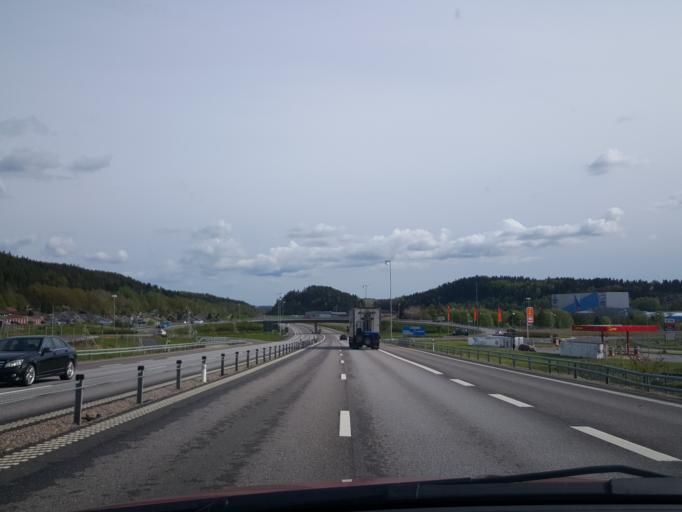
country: SE
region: Vaestra Goetaland
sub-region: Lilla Edets Kommun
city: Lilla Edet
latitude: 58.1275
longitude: 12.1366
